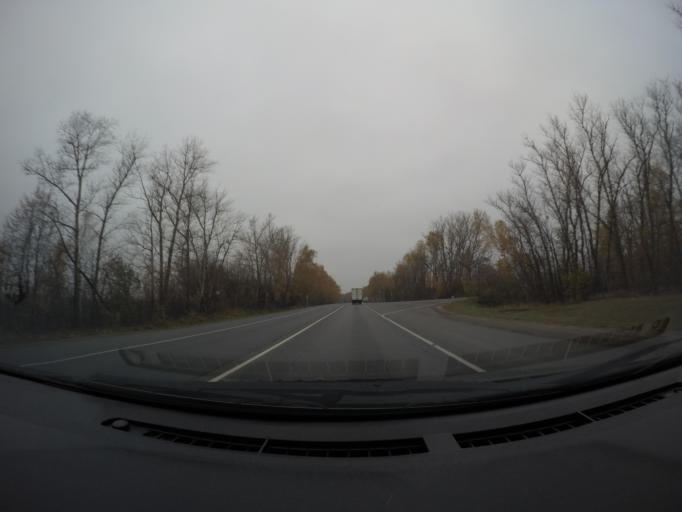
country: RU
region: Moskovskaya
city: Zhitnevo
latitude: 55.3660
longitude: 37.9848
